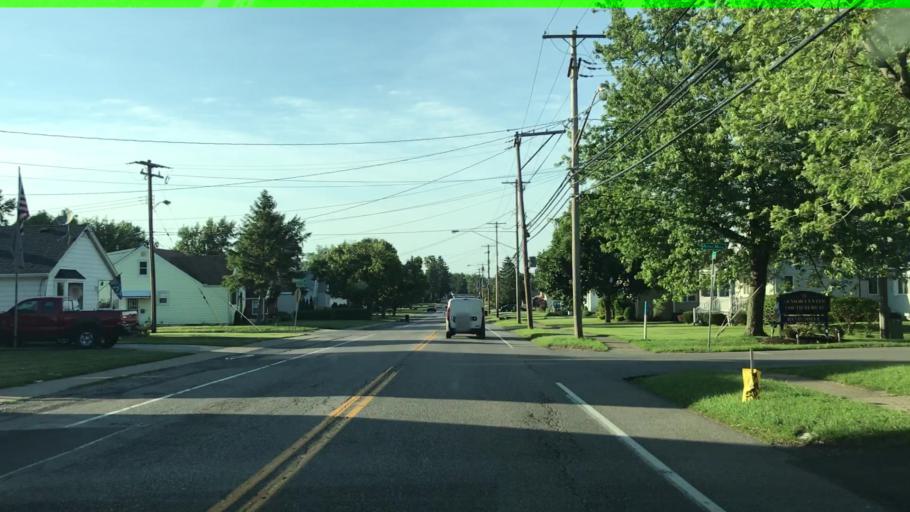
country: US
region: New York
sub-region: Erie County
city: Lancaster
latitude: 42.8886
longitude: -78.6767
